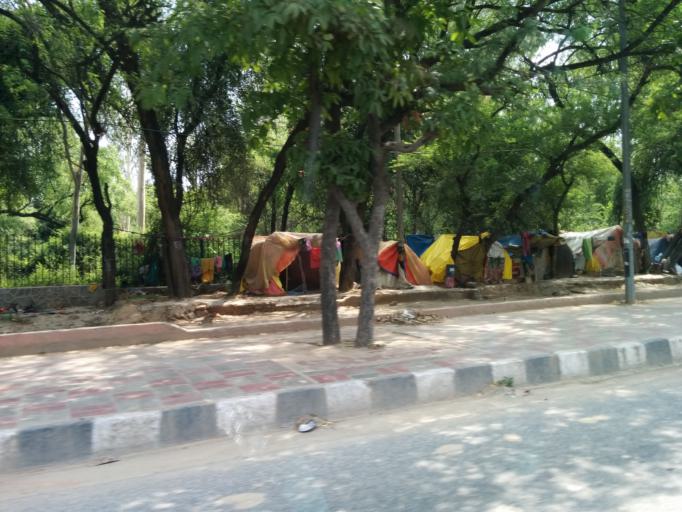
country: IN
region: NCT
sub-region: New Delhi
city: New Delhi
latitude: 28.5478
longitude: 77.1910
